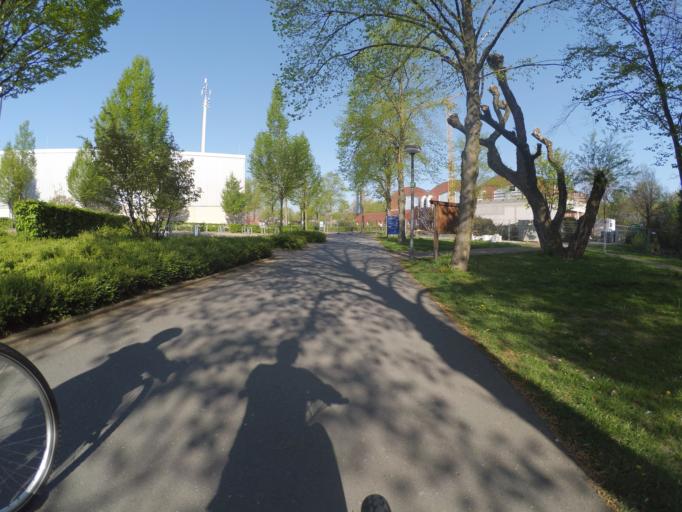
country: DE
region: North Rhine-Westphalia
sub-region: Regierungsbezirk Munster
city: Senden
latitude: 51.8541
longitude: 7.4786
